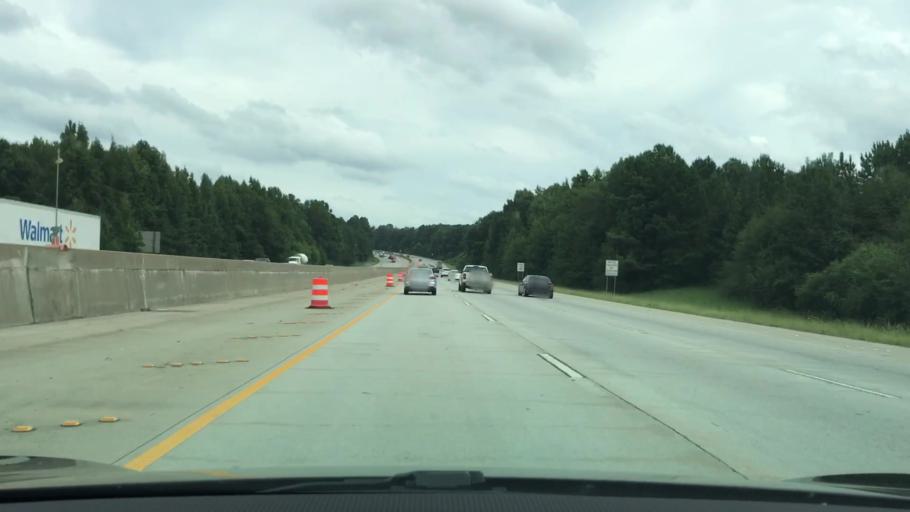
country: US
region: Georgia
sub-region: Coweta County
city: East Newnan
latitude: 33.3408
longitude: -84.7649
